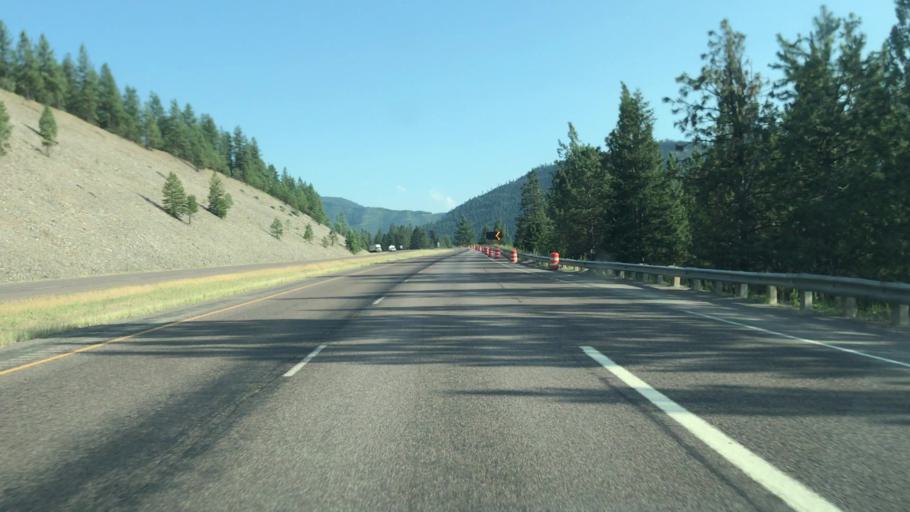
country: US
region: Montana
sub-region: Mineral County
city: Superior
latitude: 47.0214
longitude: -114.7370
